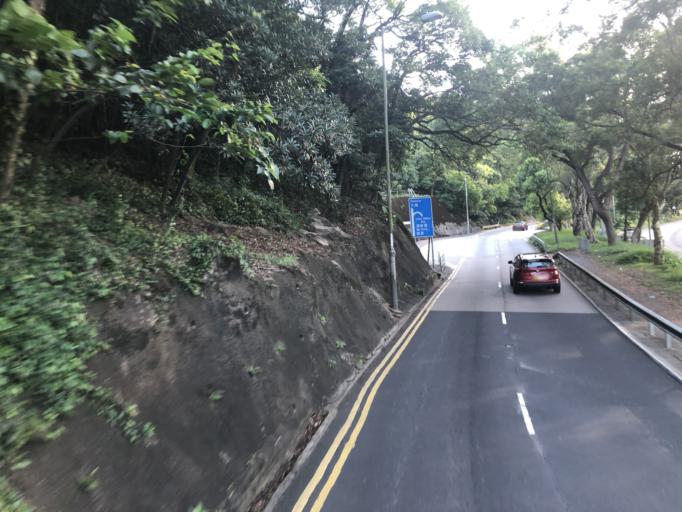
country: HK
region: Sai Kung
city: Sai Kung
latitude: 22.3434
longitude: 114.2522
